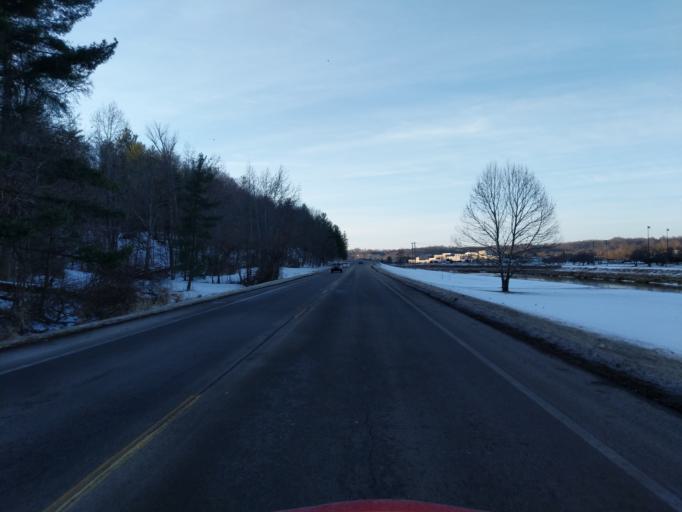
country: US
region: Ohio
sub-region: Athens County
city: Athens
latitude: 39.3216
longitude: -82.1088
